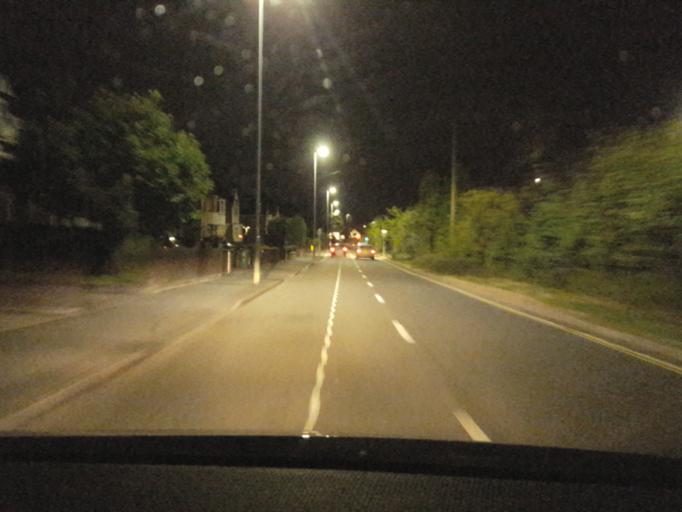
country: GB
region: England
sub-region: Leicestershire
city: Loughborough
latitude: 52.7653
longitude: -1.2144
